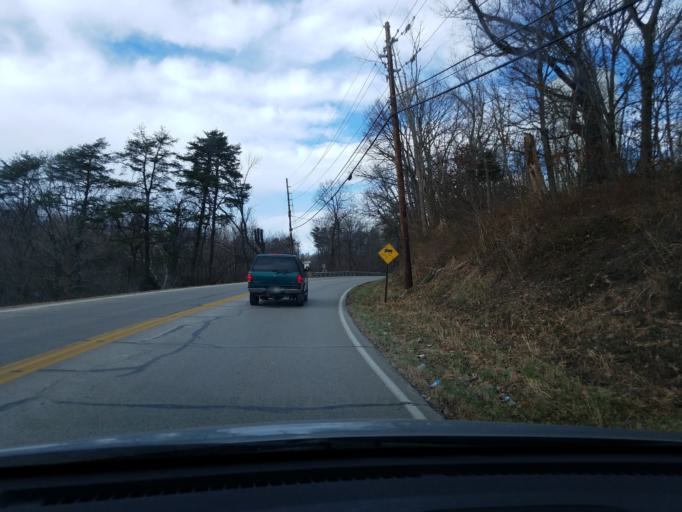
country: US
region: Indiana
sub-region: Floyd County
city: New Albany
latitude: 38.3162
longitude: -85.8535
